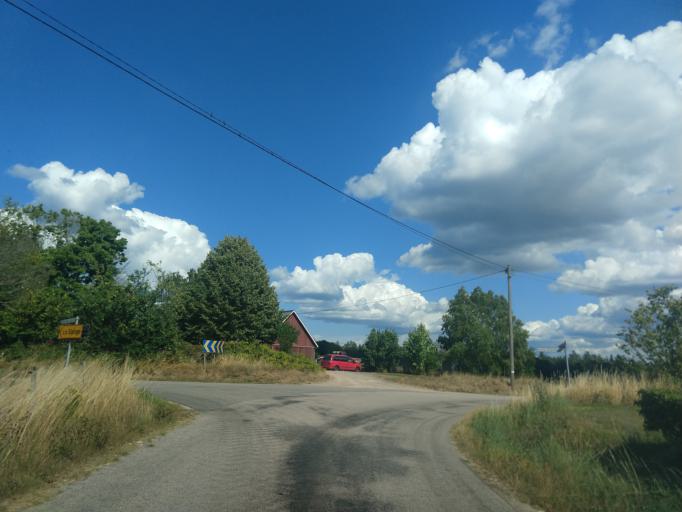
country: SE
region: Blekinge
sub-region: Ronneby Kommun
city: Brakne-Hoby
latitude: 56.2798
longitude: 15.1741
